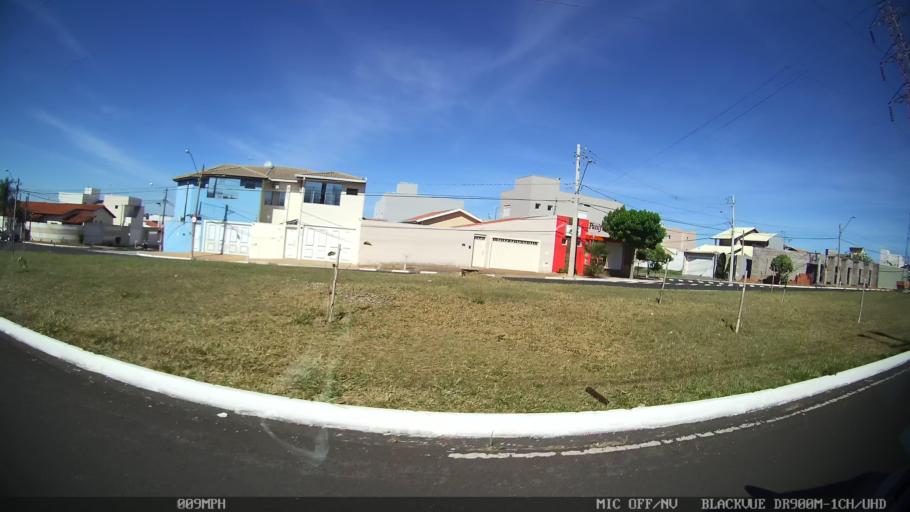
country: BR
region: Sao Paulo
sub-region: Franca
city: Franca
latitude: -20.5437
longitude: -47.3720
